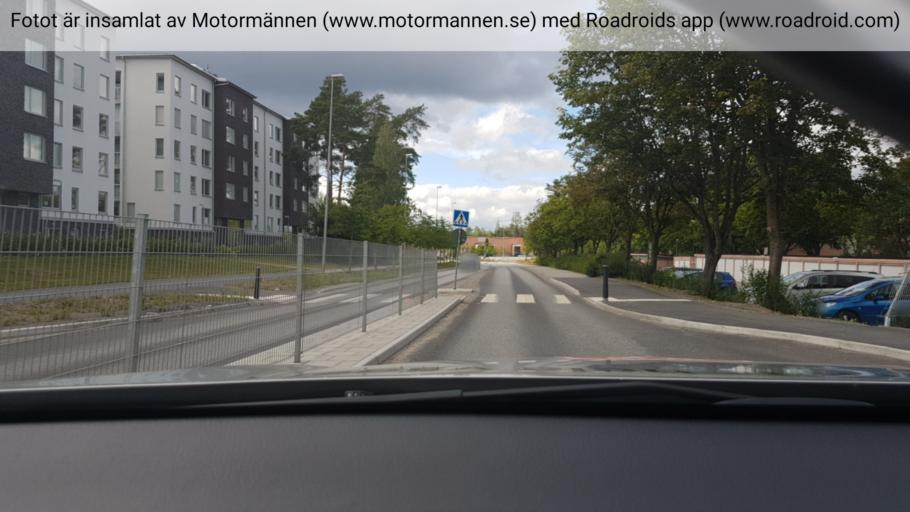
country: SE
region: Stockholm
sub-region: Tyreso Kommun
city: Bollmora
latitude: 59.2391
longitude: 18.2192
